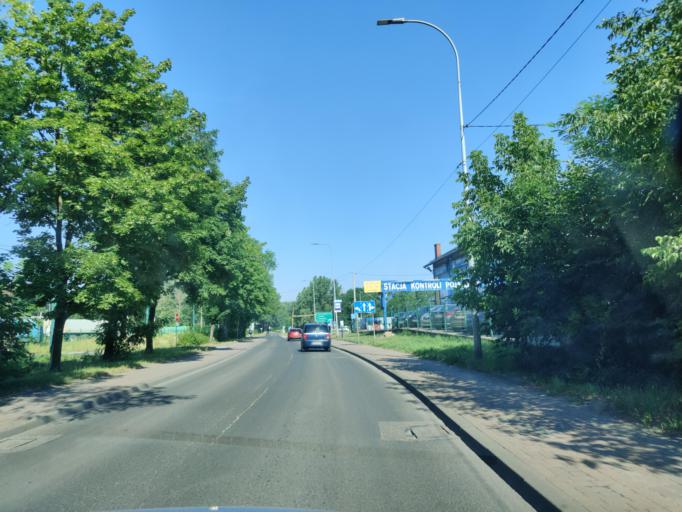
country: PL
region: Silesian Voivodeship
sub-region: Sosnowiec
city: Sosnowiec
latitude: 50.2522
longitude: 19.1277
